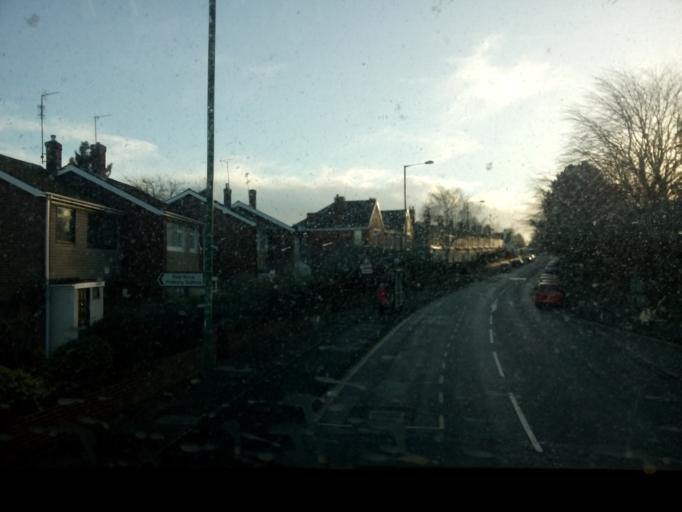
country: GB
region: England
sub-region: County Durham
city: Chester-le-Street
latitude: 54.8495
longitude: -1.5733
